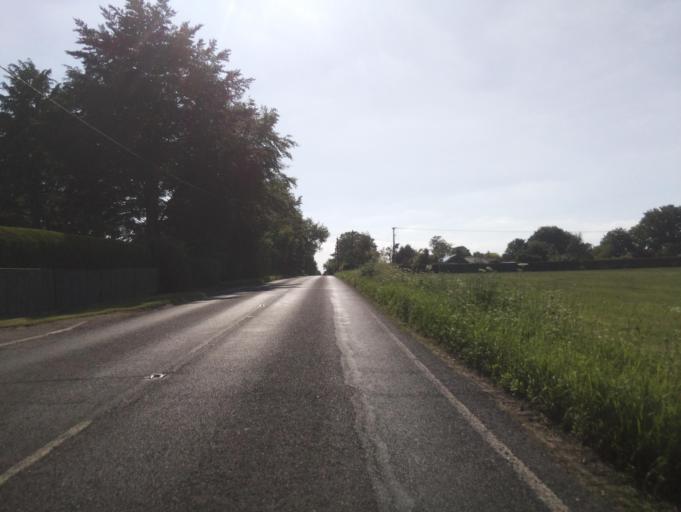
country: GB
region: England
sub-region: Hampshire
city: Andover
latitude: 51.2140
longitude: -1.4260
